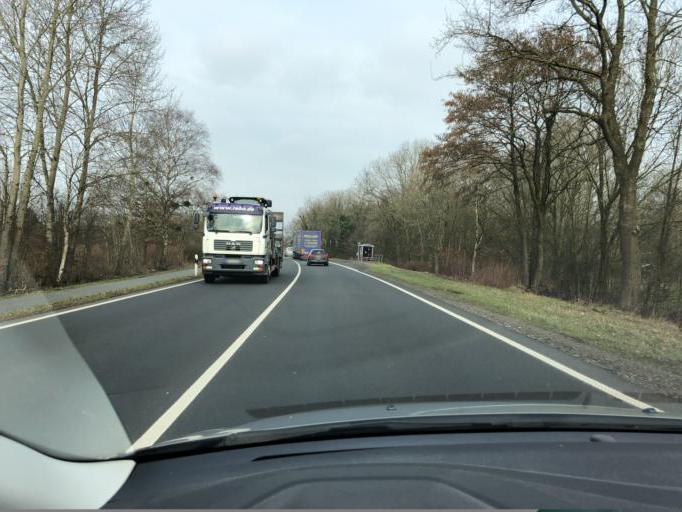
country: DE
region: Lower Saxony
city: Mittegrossefehn
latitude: 53.3872
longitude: 7.5787
